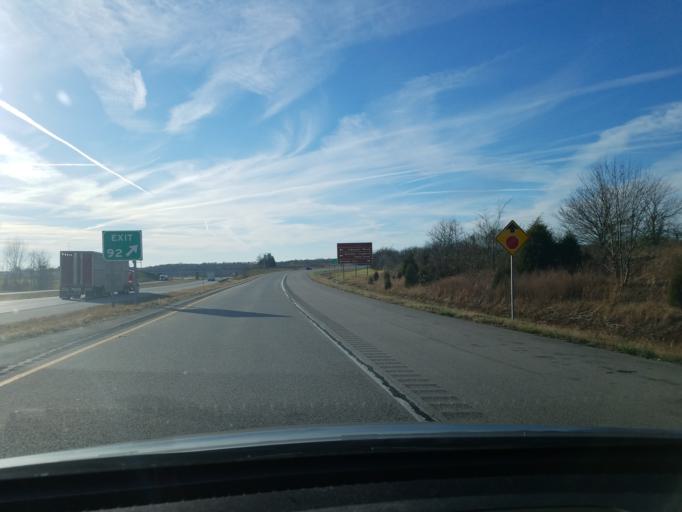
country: US
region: Indiana
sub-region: Crawford County
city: English
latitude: 38.2435
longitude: -86.3555
